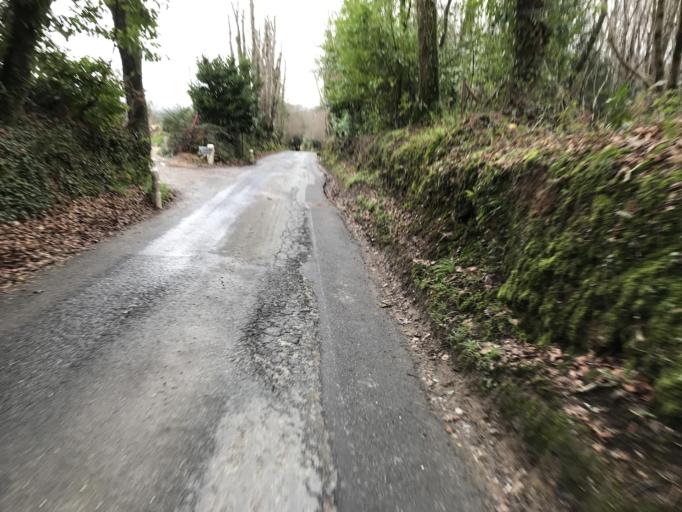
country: FR
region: Brittany
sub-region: Departement du Finistere
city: Plougastel-Daoulas
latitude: 48.3810
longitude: -4.3480
